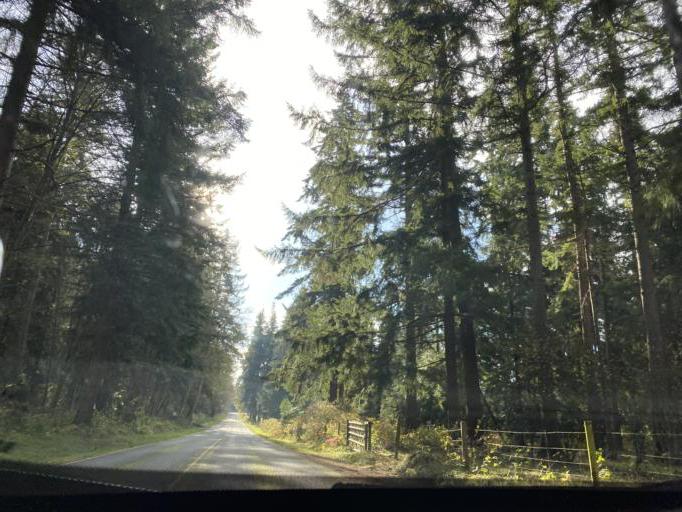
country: US
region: Washington
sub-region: Island County
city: Langley
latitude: 47.9770
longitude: -122.4513
